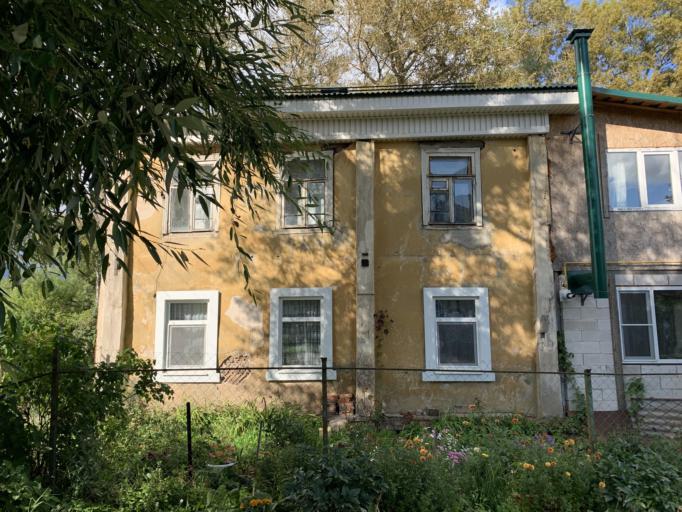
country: RU
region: Tverskaya
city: Vyshniy Volochek
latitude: 57.5758
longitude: 34.5556
